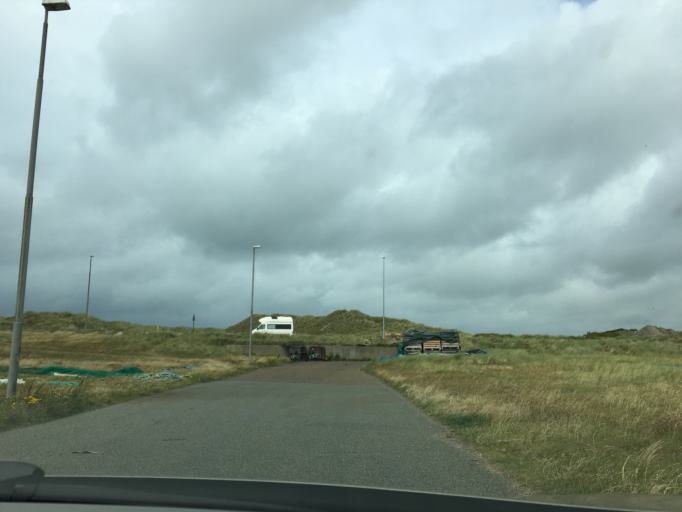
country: DK
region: Central Jutland
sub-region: Ringkobing-Skjern Kommune
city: Hvide Sande
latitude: 56.0061
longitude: 8.1228
